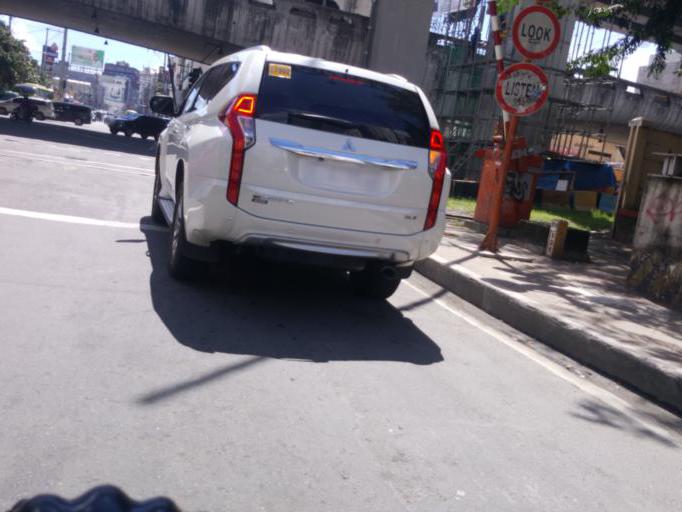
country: PH
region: Metro Manila
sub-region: Makati City
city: Makati City
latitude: 14.5584
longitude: 121.0076
